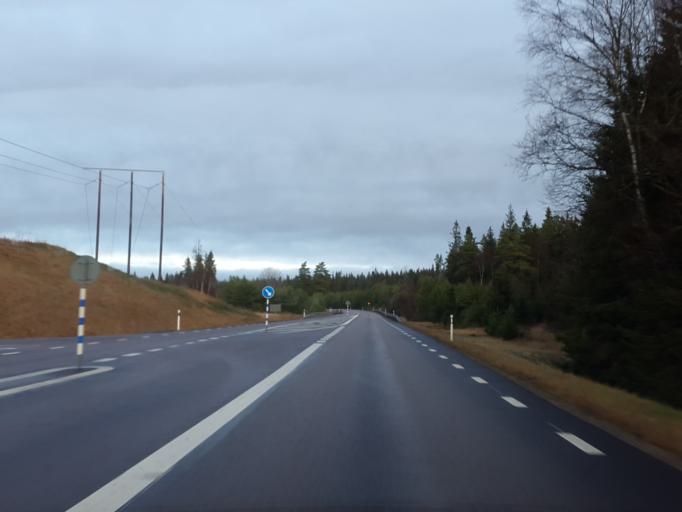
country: SE
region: Vaestra Goetaland
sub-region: Boras Kommun
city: Sandared
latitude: 57.7901
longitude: 12.7712
